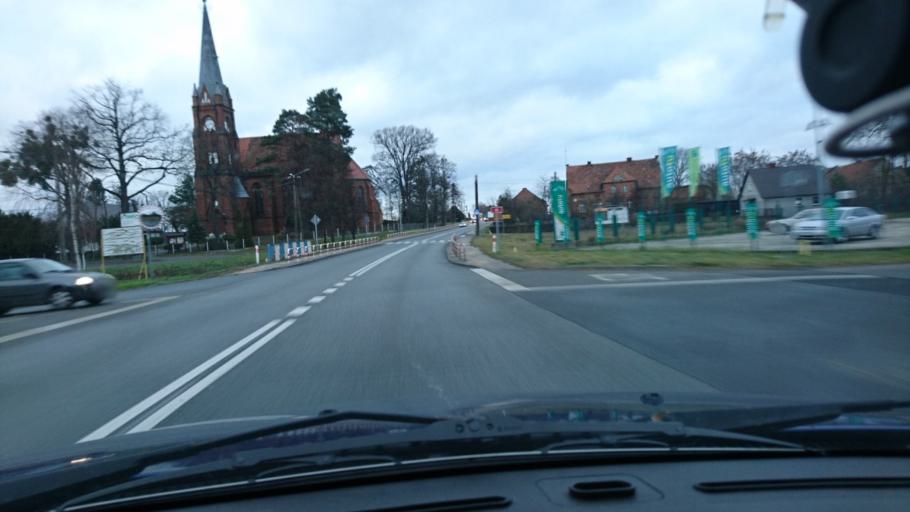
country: PL
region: Opole Voivodeship
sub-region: Powiat kluczborski
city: Kluczbork
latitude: 51.0276
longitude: 18.1919
